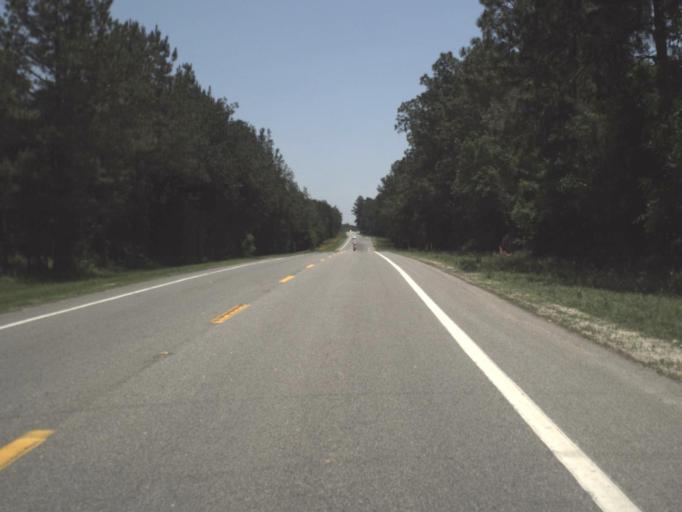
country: US
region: Florida
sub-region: Suwannee County
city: Live Oak
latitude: 30.3508
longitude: -83.1068
